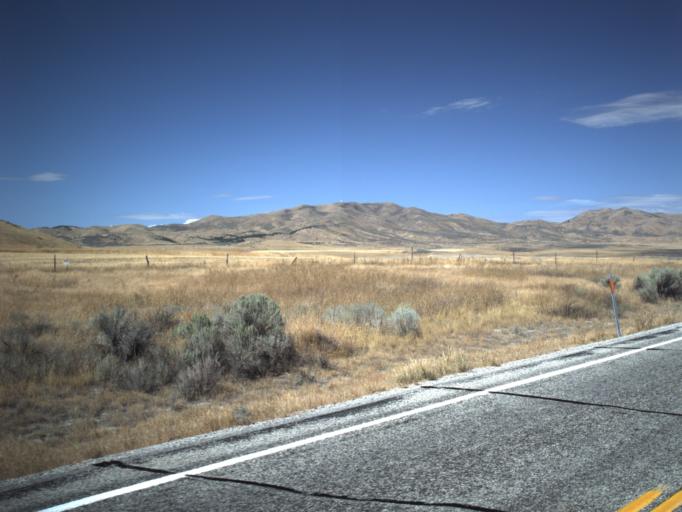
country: US
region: Utah
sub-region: Box Elder County
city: Tremonton
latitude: 41.7099
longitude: -112.4519
